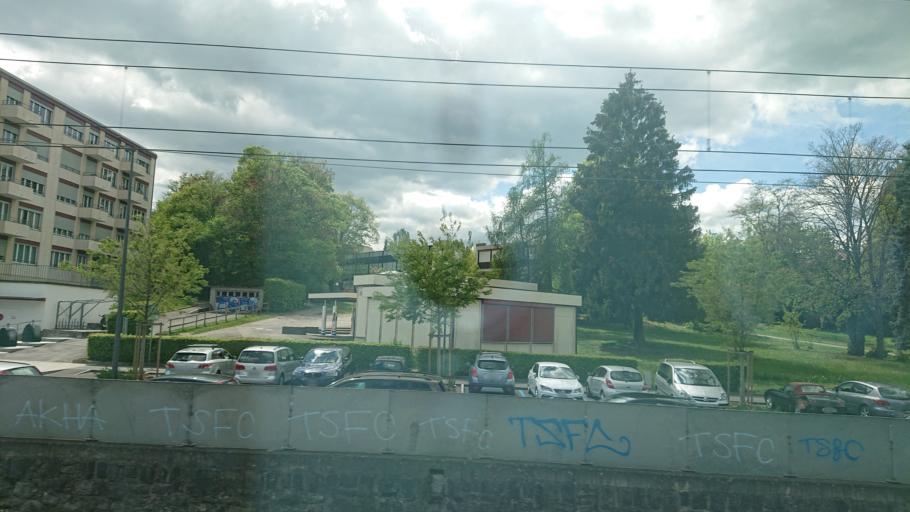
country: CH
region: Geneva
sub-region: Geneva
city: Versoix
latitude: 46.2804
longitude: 6.1652
